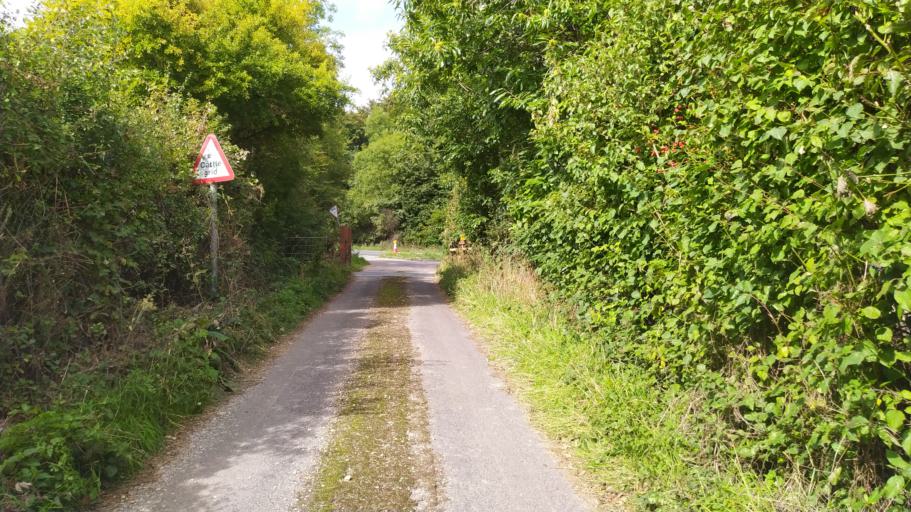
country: GB
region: England
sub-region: Hampshire
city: Long Sutton
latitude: 51.1825
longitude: -0.9035
